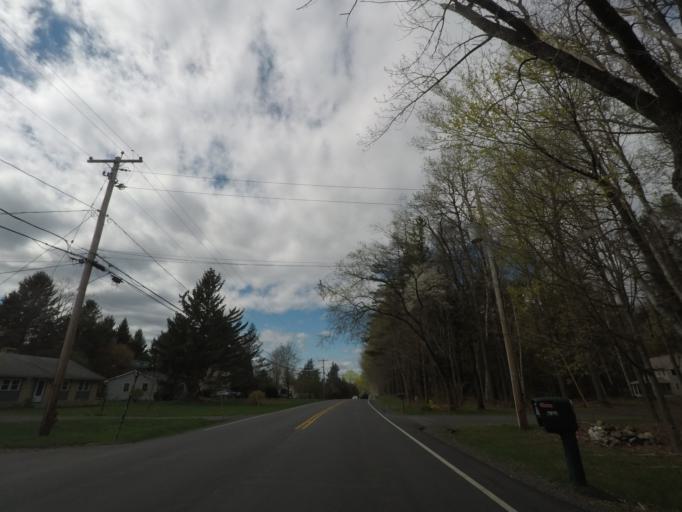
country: US
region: New York
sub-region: Columbia County
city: Valatie
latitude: 42.4043
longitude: -73.6736
